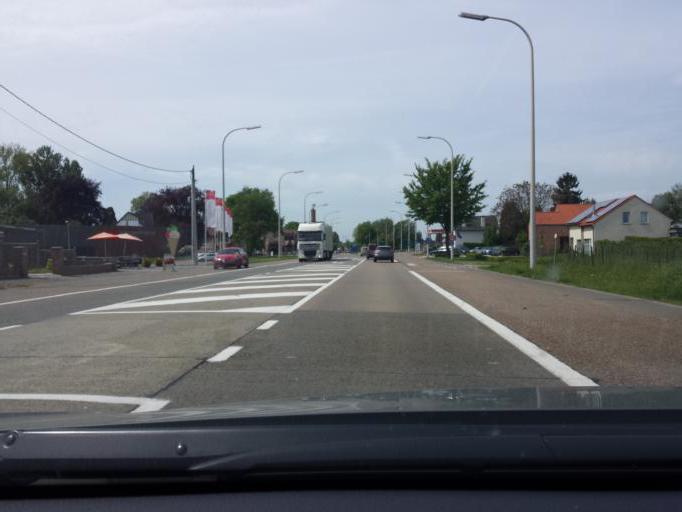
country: BE
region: Flanders
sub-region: Provincie Limburg
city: Halen
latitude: 50.9484
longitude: 5.1232
